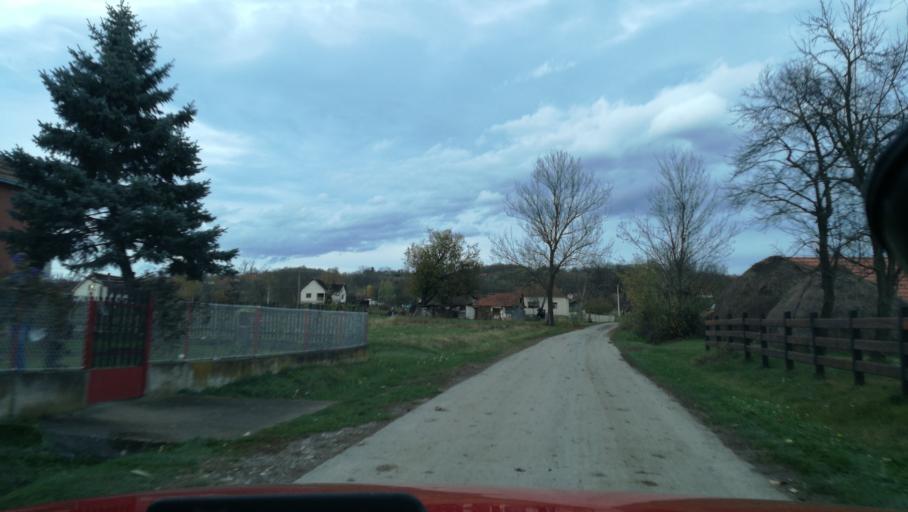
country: RS
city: Prislonica
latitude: 43.9077
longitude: 20.4377
